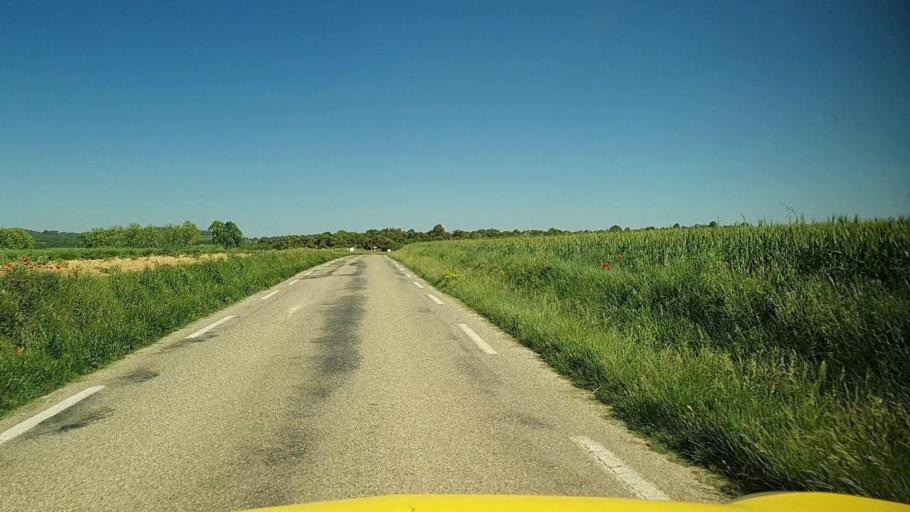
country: FR
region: Languedoc-Roussillon
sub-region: Departement du Gard
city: Saint-Chaptes
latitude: 43.9824
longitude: 4.2745
